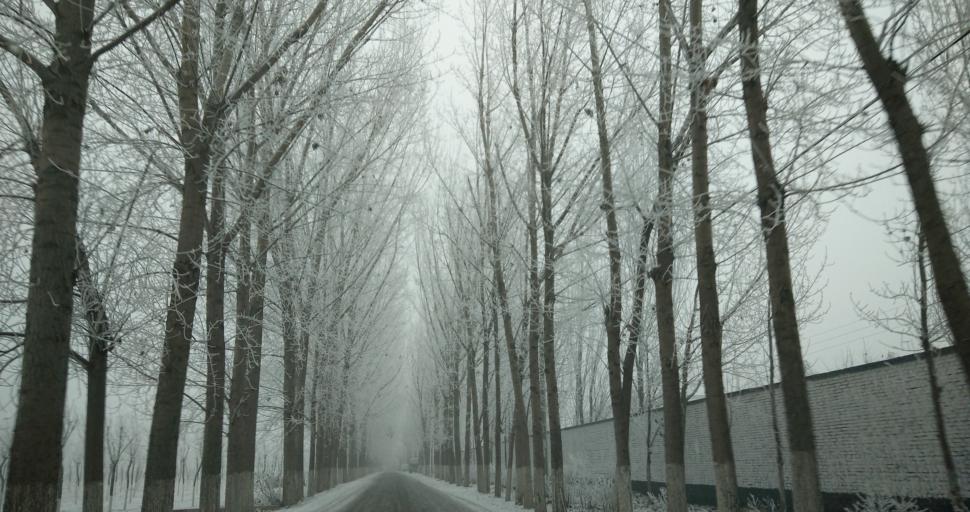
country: CN
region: Beijing
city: Yinghai
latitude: 39.7146
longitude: 116.4277
